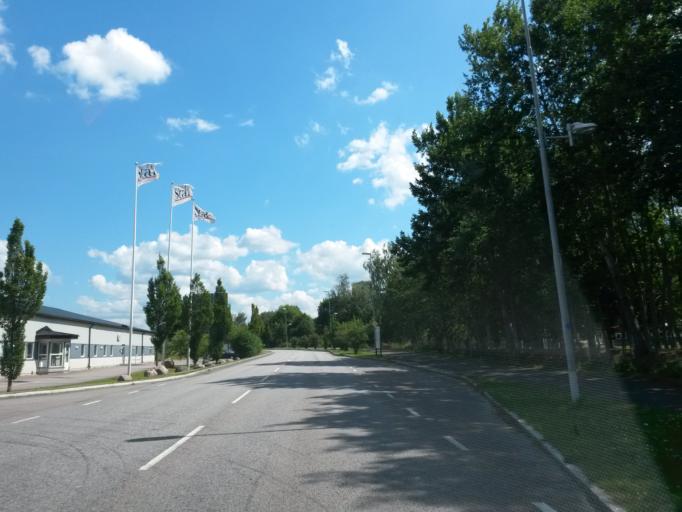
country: SE
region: Vaestra Goetaland
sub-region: Lerums Kommun
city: Stenkullen
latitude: 57.7960
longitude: 12.3089
